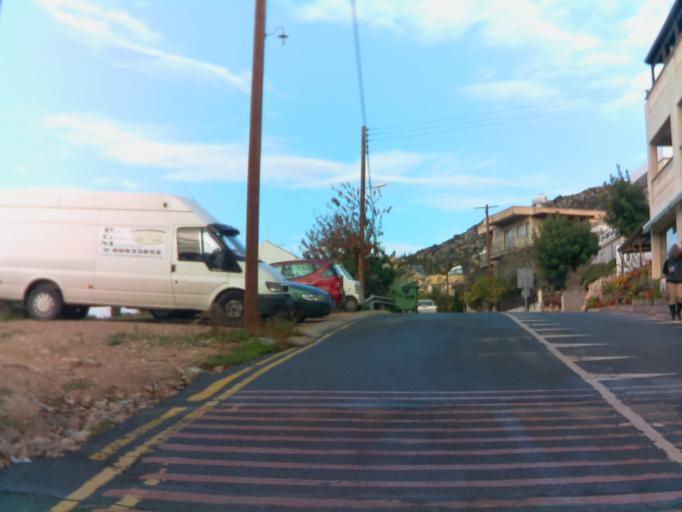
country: CY
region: Pafos
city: Pegeia
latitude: 34.8845
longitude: 32.3800
